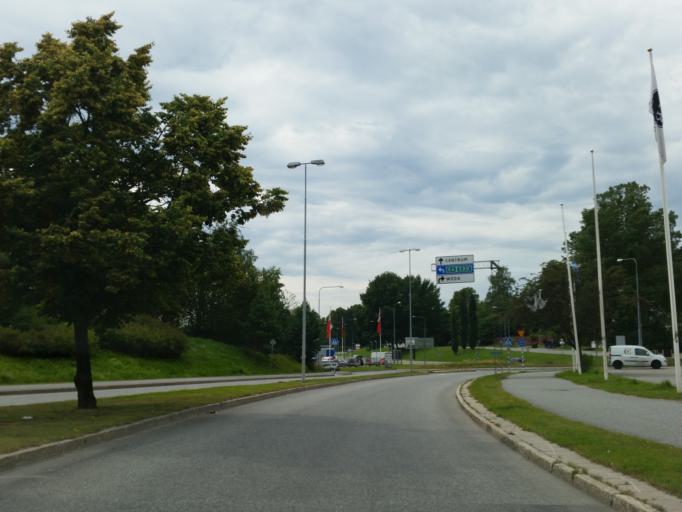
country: SE
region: Stockholm
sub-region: Sodertalje Kommun
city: Soedertaelje
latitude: 59.2048
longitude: 17.6458
